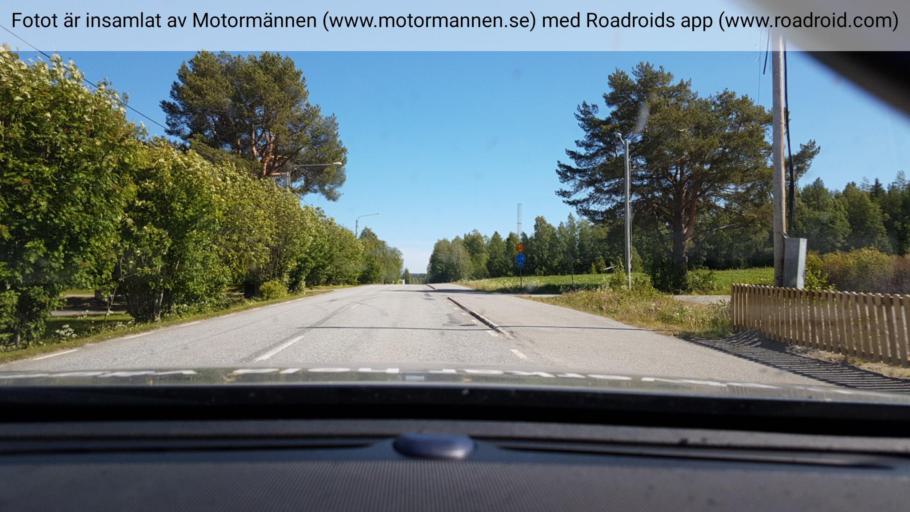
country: SE
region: Vaesterbotten
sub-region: Vilhelmina Kommun
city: Sjoberg
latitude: 64.6382
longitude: 16.3640
